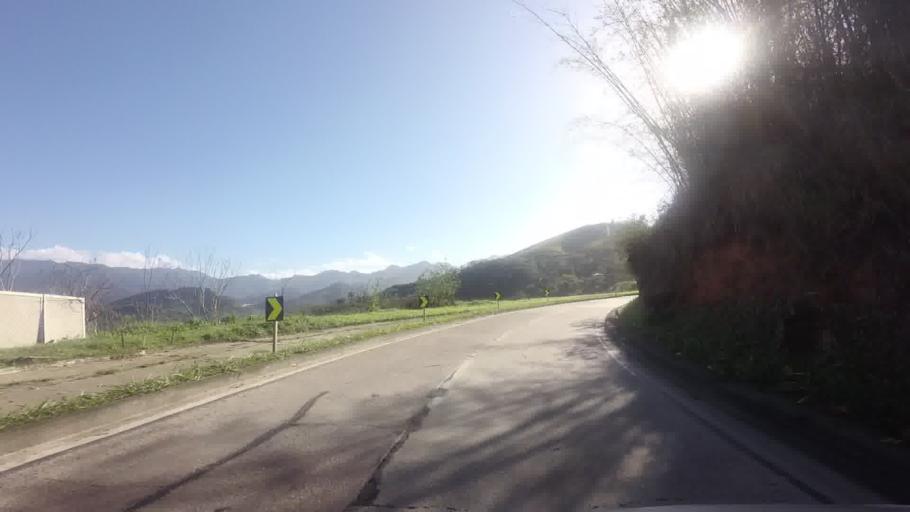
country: BR
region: Rio de Janeiro
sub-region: Petropolis
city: Petropolis
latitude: -22.5920
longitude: -43.2775
